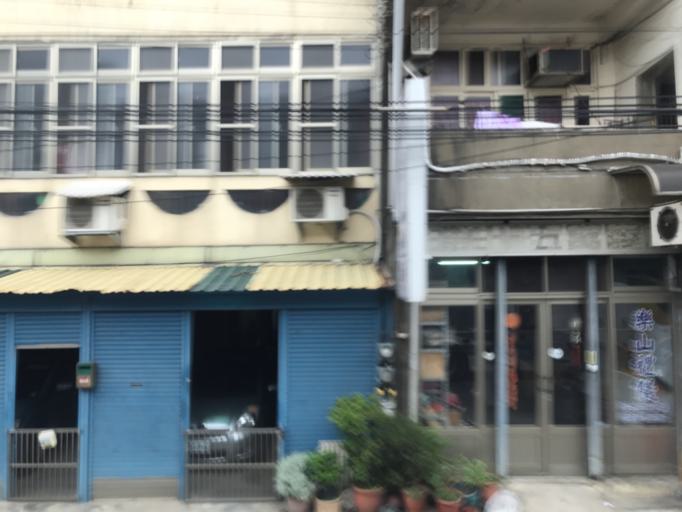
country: TW
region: Taiwan
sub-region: Hsinchu
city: Hsinchu
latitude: 24.8364
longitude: 120.9438
